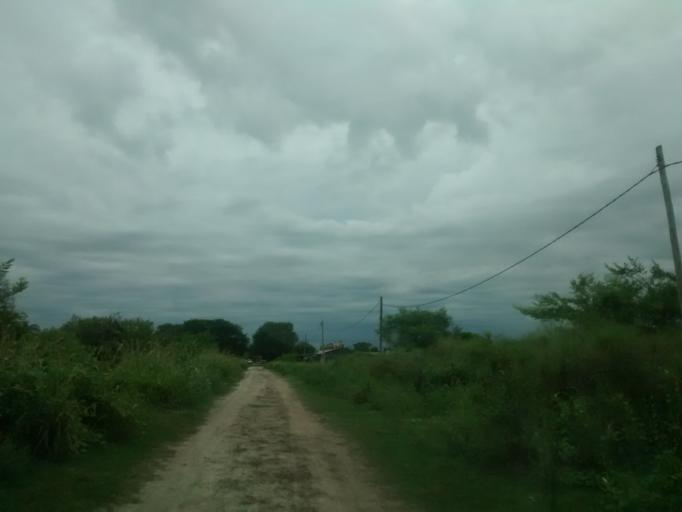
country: AR
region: Chaco
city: Puerto Tirol
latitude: -27.3755
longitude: -59.0998
